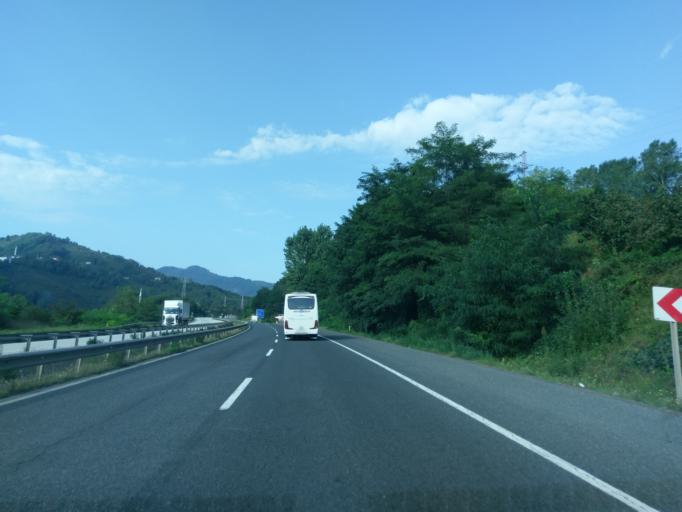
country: TR
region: Ordu
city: Persembe
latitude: 40.9822
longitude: 37.7590
